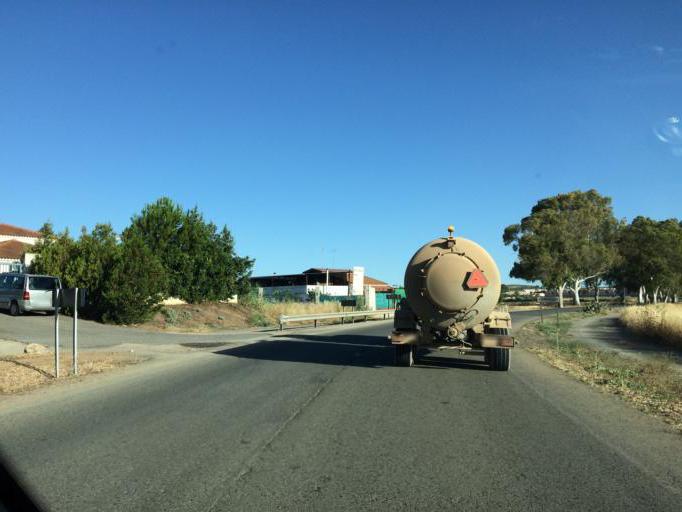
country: ES
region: Andalusia
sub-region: Provincia de Malaga
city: Campillos
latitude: 37.0354
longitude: -4.8569
